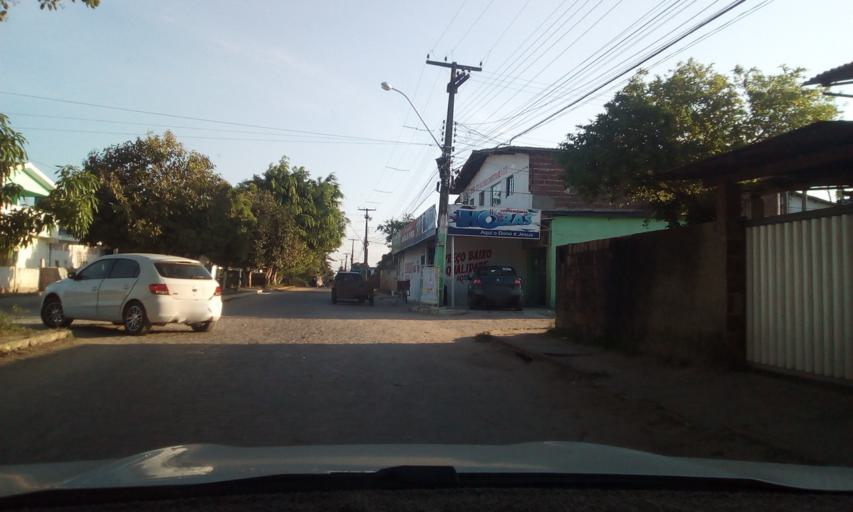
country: BR
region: Paraiba
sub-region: Bayeux
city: Bayeux
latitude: -7.1800
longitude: -34.9332
